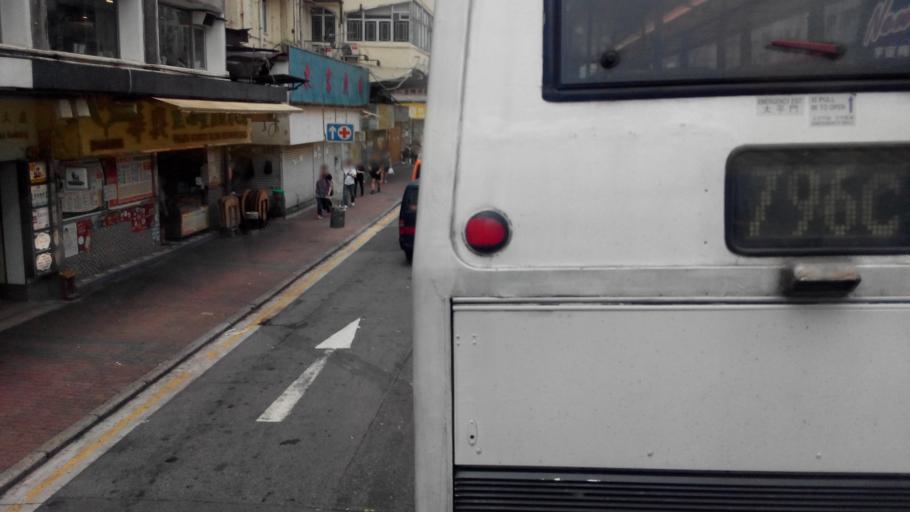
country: HK
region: Sham Shui Po
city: Sham Shui Po
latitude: 22.3361
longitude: 114.1584
